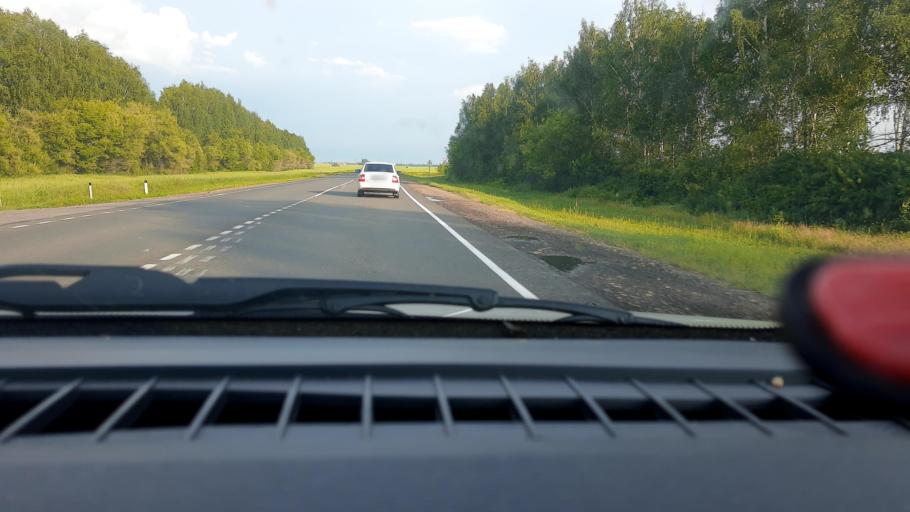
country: RU
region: Nizjnij Novgorod
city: Shatki
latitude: 55.2274
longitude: 44.0664
